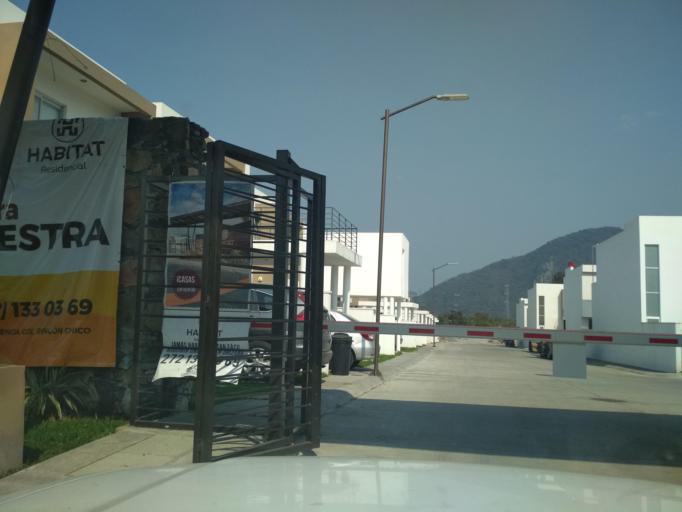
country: MX
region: Veracruz
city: Jalapilla
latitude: 18.8377
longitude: -97.0856
